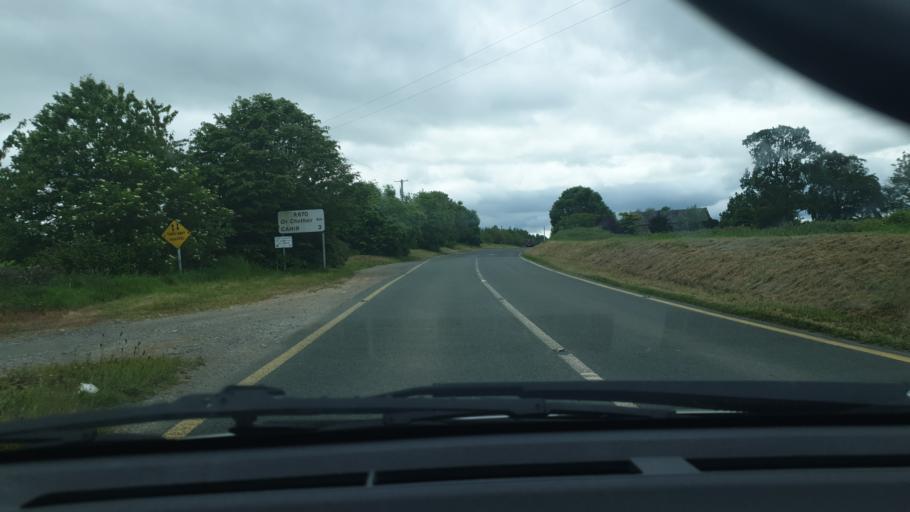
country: IE
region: Munster
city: Cahir
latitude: 52.3945
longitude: -7.9110
